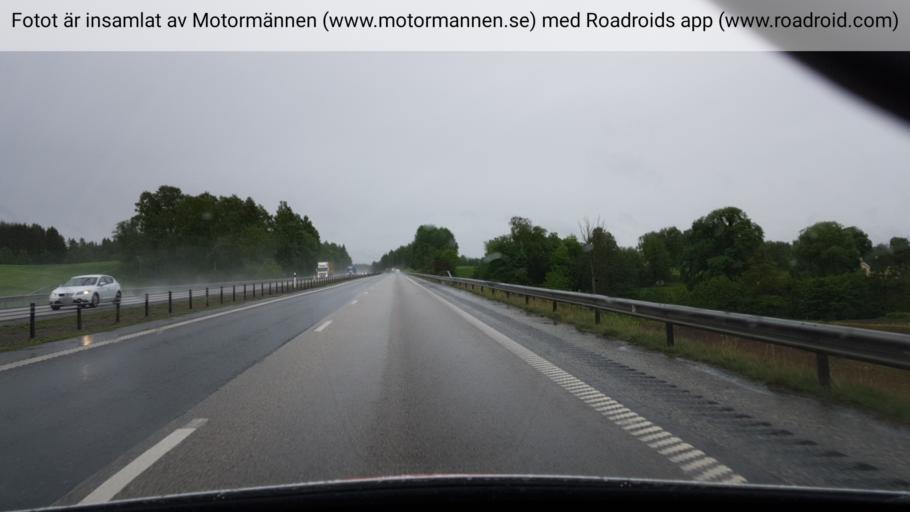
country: SE
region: Joenkoeping
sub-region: Jonkopings Kommun
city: Odensjo
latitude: 57.7350
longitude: 14.1582
